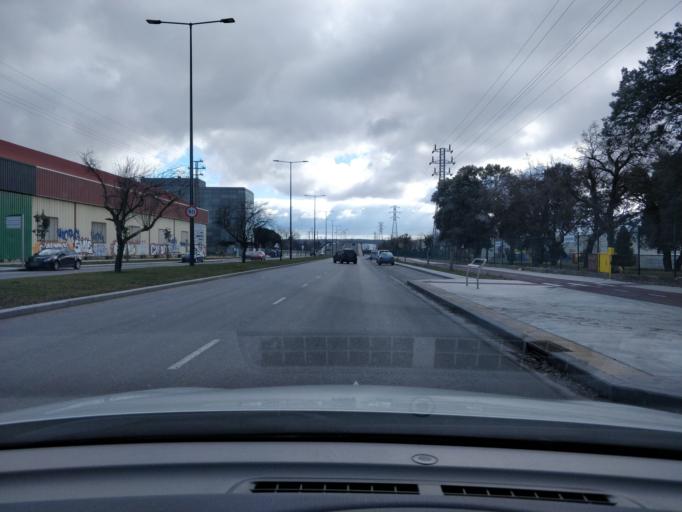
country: ES
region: Castille and Leon
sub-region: Provincia de Burgos
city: Burgos
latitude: 42.3576
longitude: -3.6509
